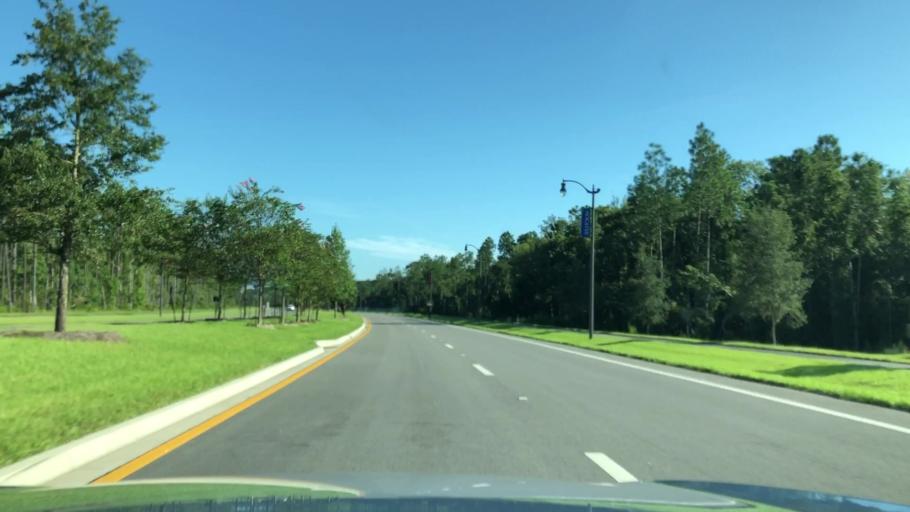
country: US
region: Florida
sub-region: Saint Johns County
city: Palm Valley
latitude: 30.0872
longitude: -81.4056
